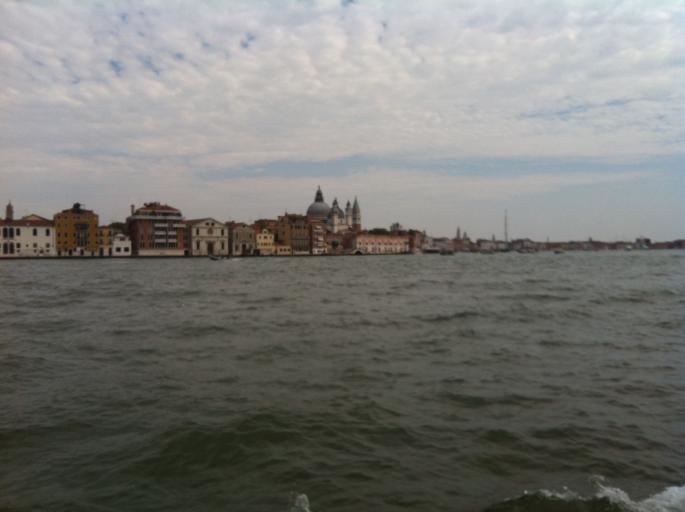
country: IT
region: Veneto
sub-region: Provincia di Venezia
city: Giudecca
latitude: 45.4261
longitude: 12.3303
